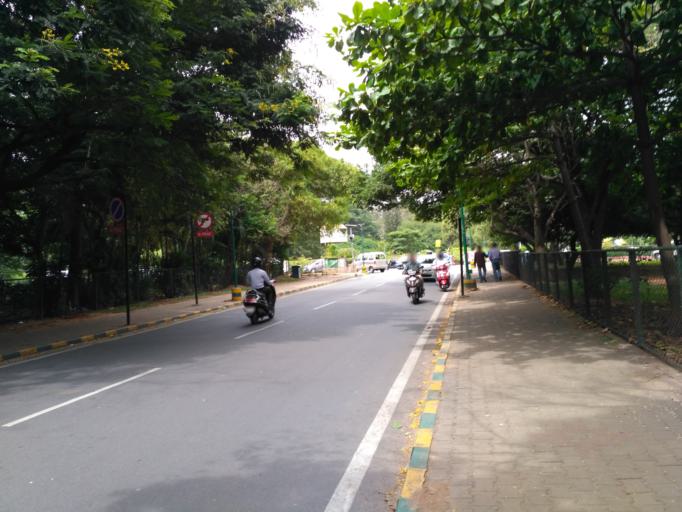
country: IN
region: Karnataka
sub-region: Bangalore Urban
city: Bangalore
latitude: 12.9749
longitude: 77.5899
